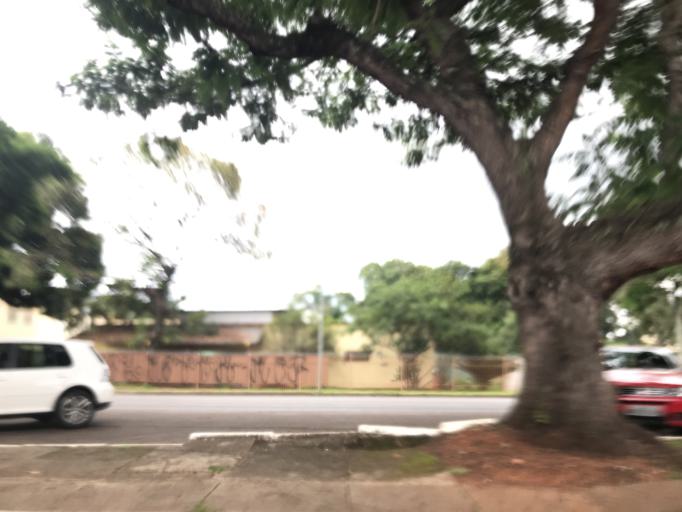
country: BR
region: Federal District
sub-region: Brasilia
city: Brasilia
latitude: -15.8221
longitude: -47.9194
